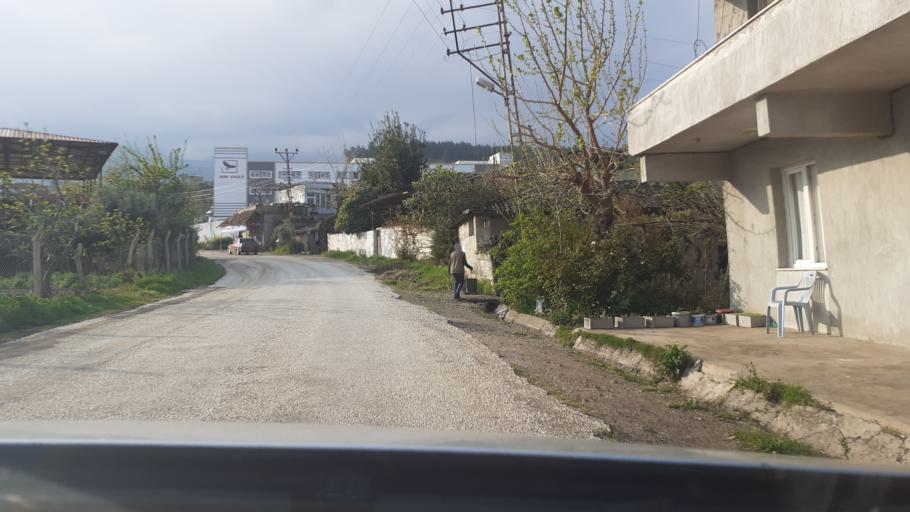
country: TR
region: Hatay
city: Kirikhan
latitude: 36.5006
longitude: 36.3315
